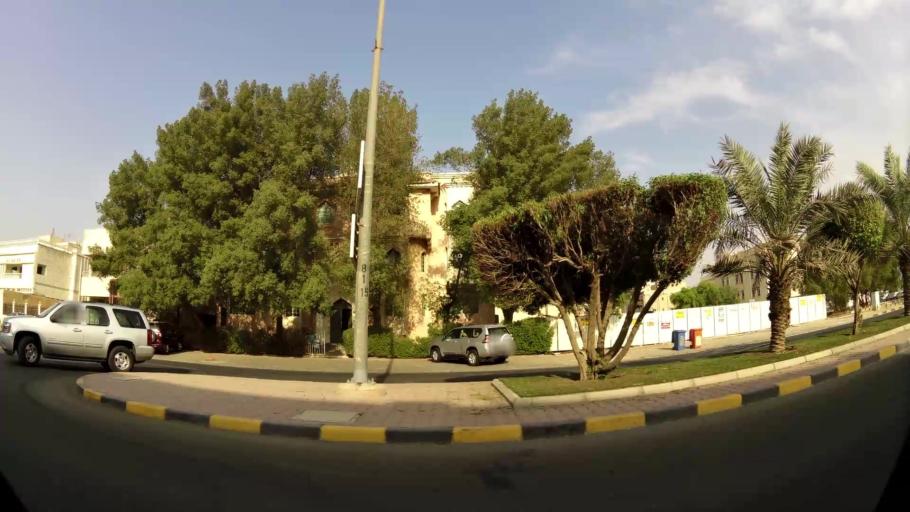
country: KW
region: Al Asimah
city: Ad Dasmah
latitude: 29.3364
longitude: 47.9956
